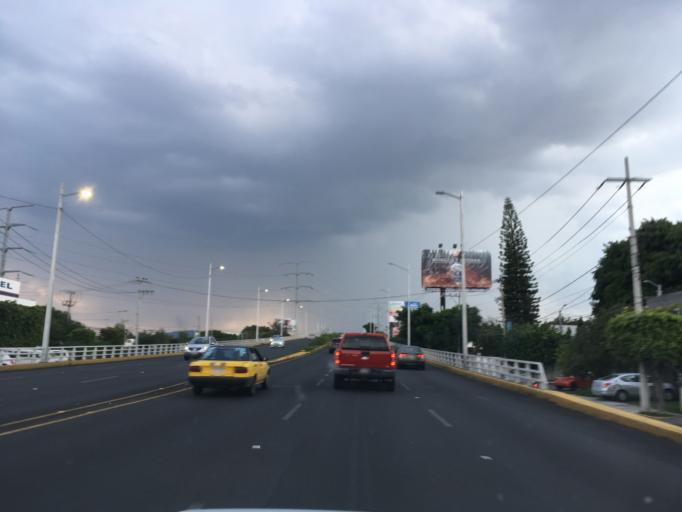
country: MX
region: Jalisco
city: Guadalajara
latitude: 20.6745
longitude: -103.3966
